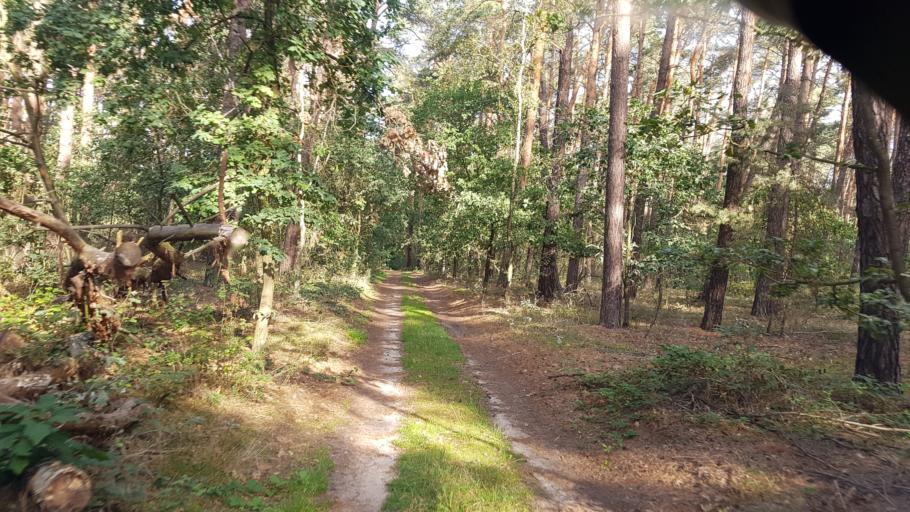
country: DE
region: Brandenburg
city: Finsterwalde
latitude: 51.6679
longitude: 13.6858
